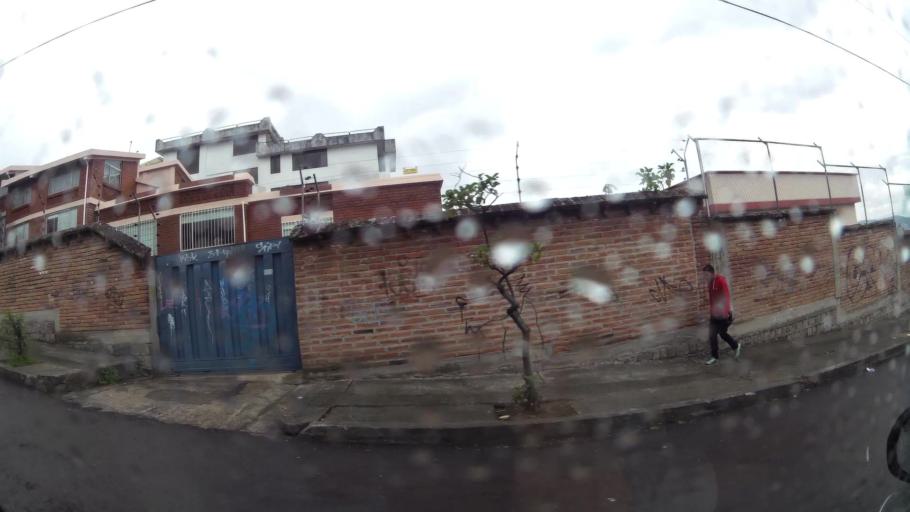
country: EC
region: Pichincha
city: Quito
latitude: -0.1981
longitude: -78.5101
